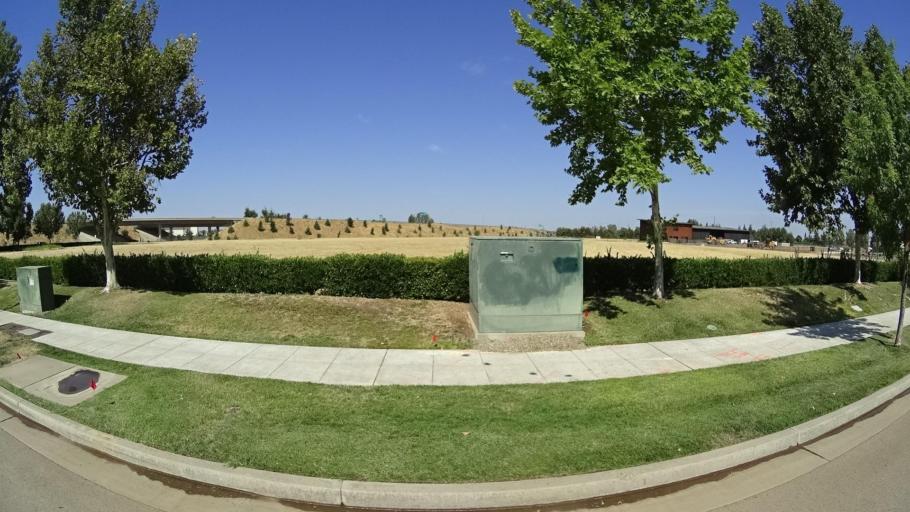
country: US
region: California
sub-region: Fresno County
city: Sunnyside
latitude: 36.7519
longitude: -119.6724
